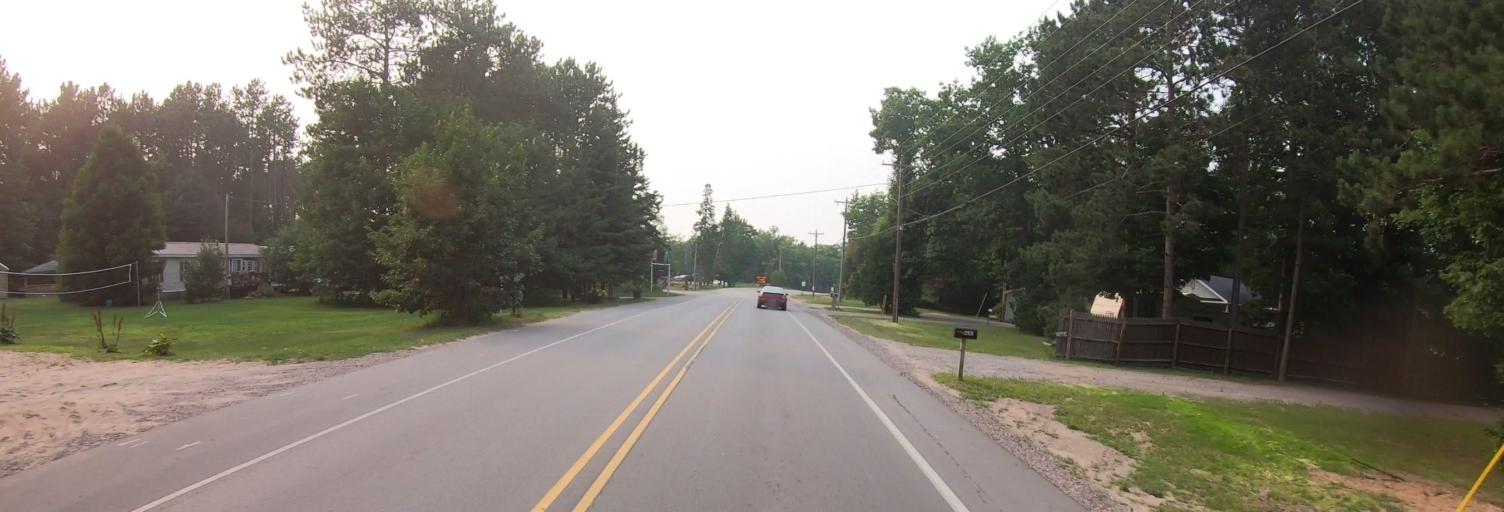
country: US
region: Michigan
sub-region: Chippewa County
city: Sault Ste. Marie
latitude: 46.4608
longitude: -84.6175
